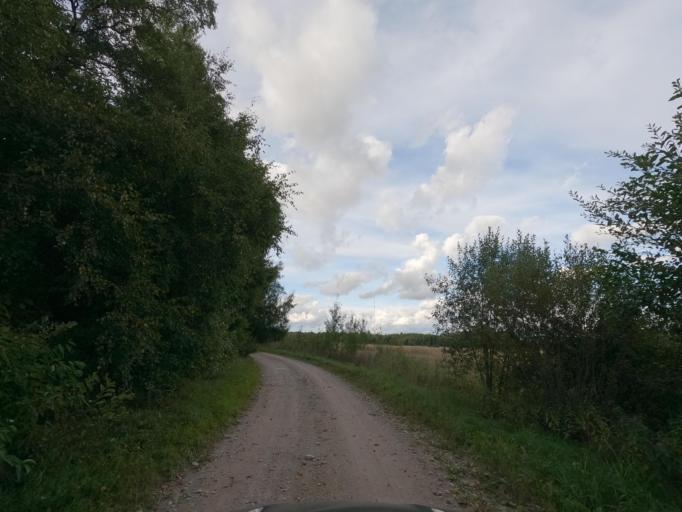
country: EE
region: Raplamaa
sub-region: Rapla vald
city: Rapla
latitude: 59.0141
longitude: 24.7658
